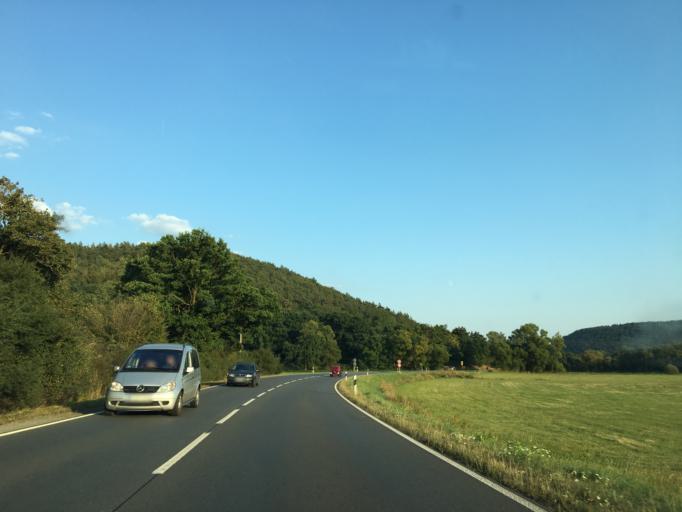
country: DE
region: Hesse
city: Wetter
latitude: 50.8809
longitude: 8.7648
